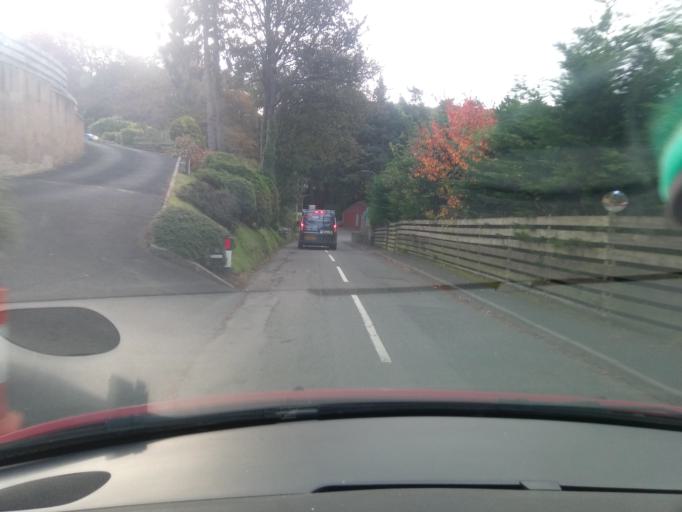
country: GB
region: Scotland
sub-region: The Scottish Borders
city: Galashiels
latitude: 55.6929
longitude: -2.8598
